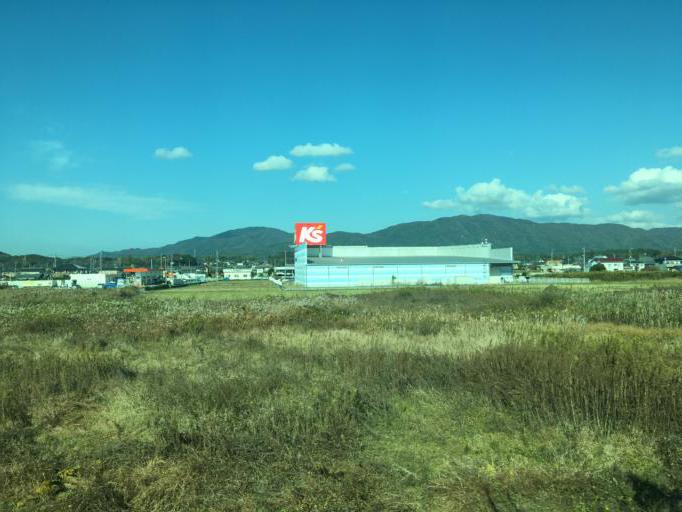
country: JP
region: Ibaraki
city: Iwase
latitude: 36.3556
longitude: 140.1390
